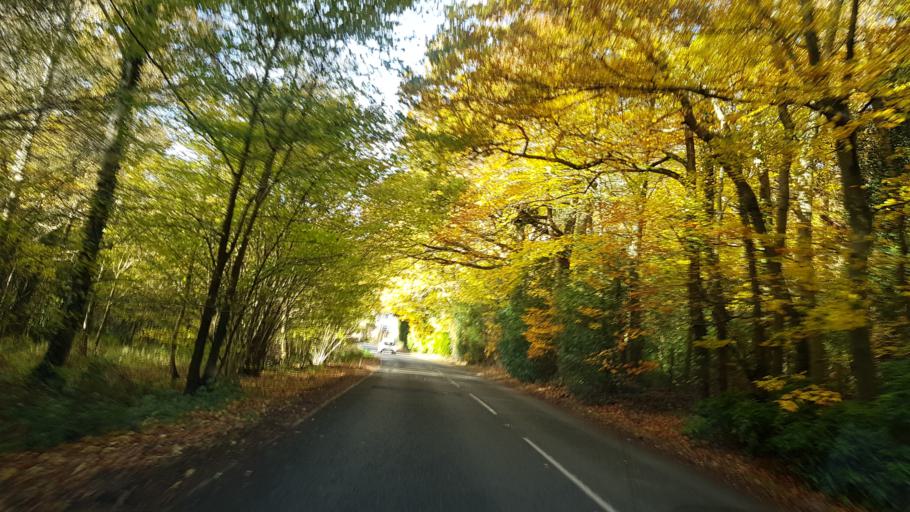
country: GB
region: England
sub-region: Surrey
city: Elstead
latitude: 51.1906
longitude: -0.7200
